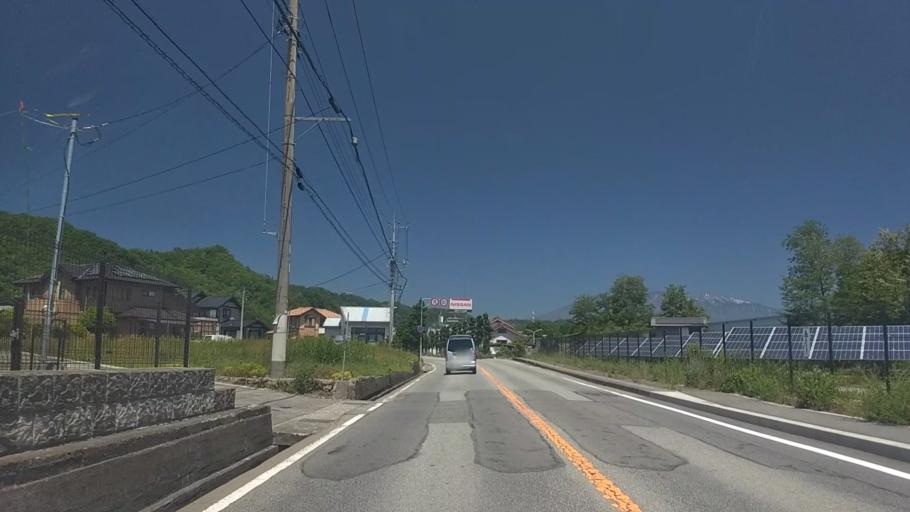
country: JP
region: Yamanashi
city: Nirasaki
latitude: 35.7640
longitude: 138.4282
